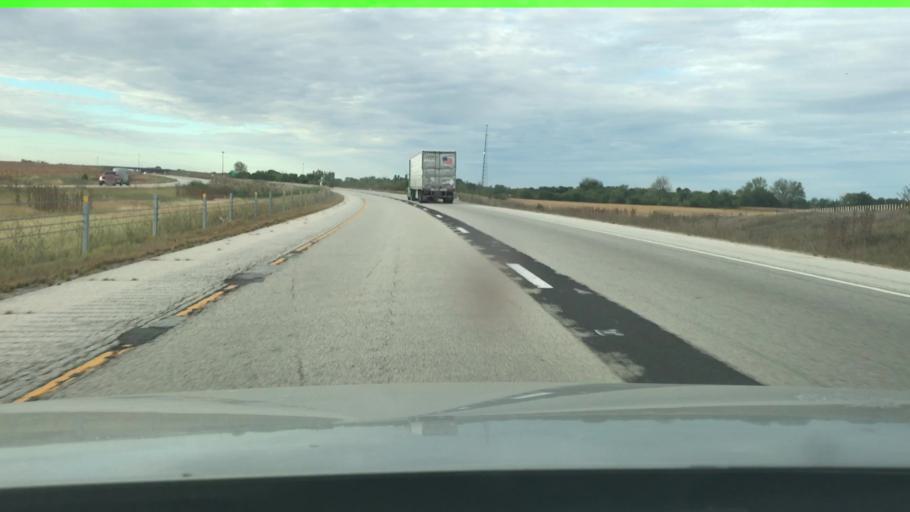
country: US
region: Illinois
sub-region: Livingston County
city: Odell
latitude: 41.0162
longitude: -88.5329
